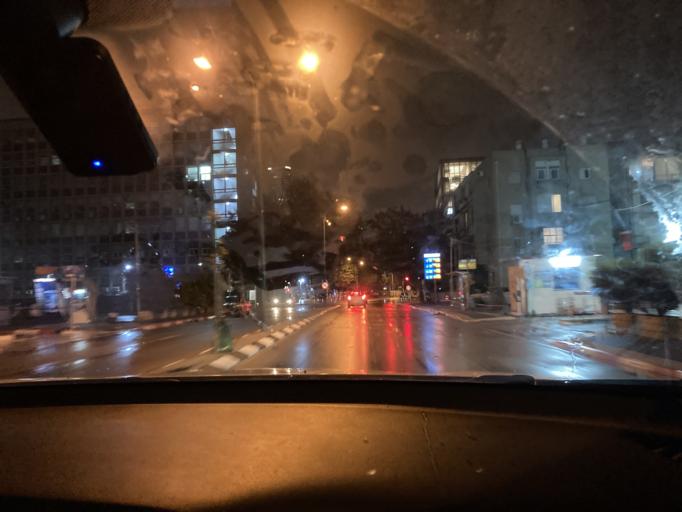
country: IL
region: Tel Aviv
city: Tel Aviv
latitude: 32.0744
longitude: 34.7835
